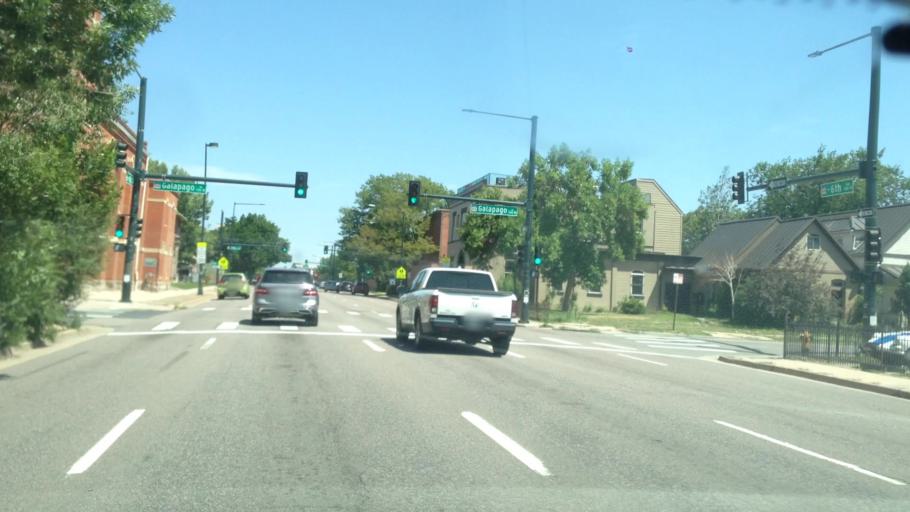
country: US
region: Colorado
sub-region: Denver County
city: Denver
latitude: 39.7257
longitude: -104.9967
